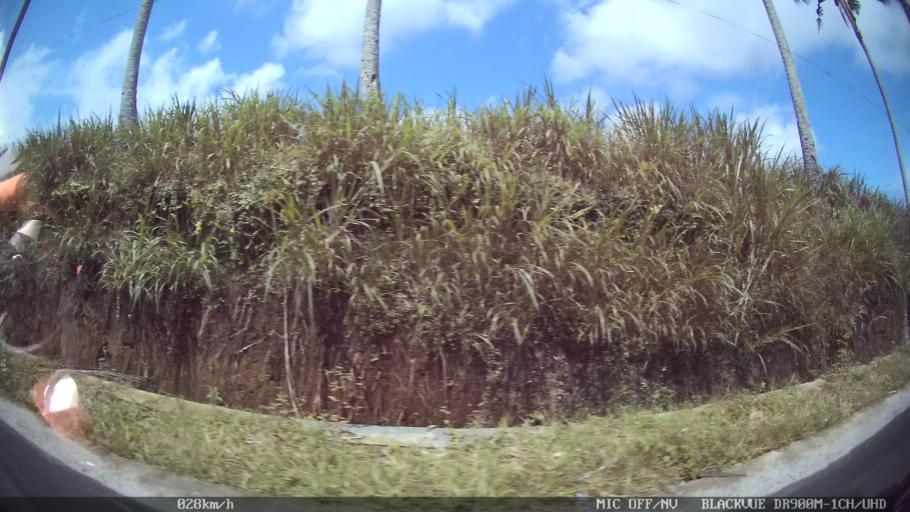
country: ID
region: Bali
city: Banjar Apuan Kaja
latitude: -8.4930
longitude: 115.3418
